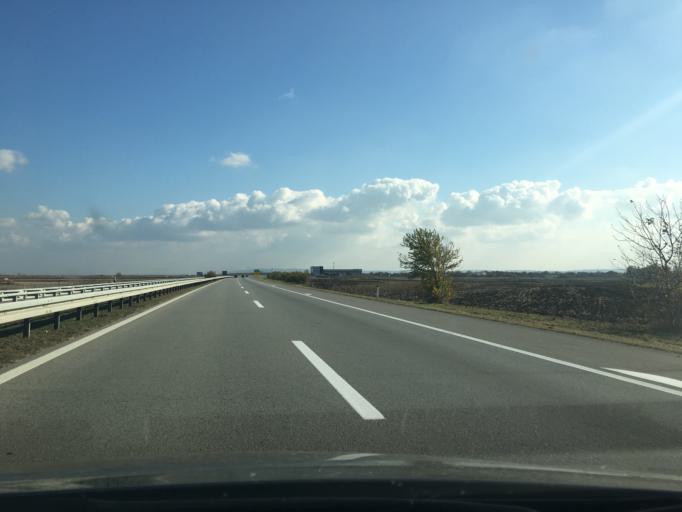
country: RS
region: Autonomna Pokrajina Vojvodina
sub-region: Juznobacki Okrug
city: Kovilj
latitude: 45.2502
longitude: 20.0205
